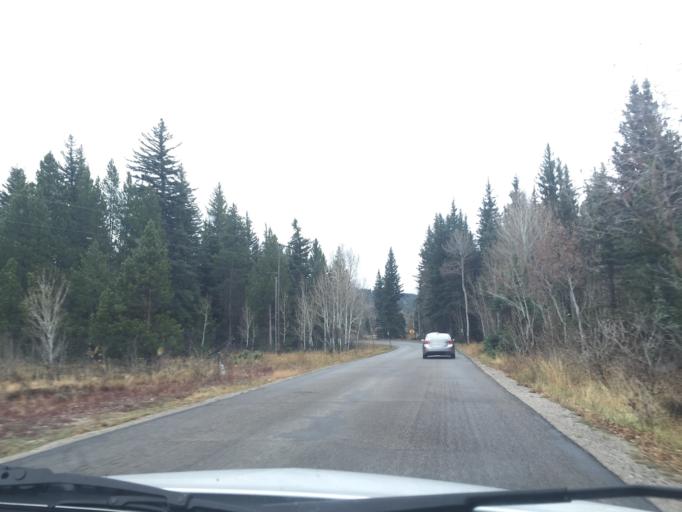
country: US
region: Wyoming
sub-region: Teton County
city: Moose Wilson Road
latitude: 43.6571
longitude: -110.7215
